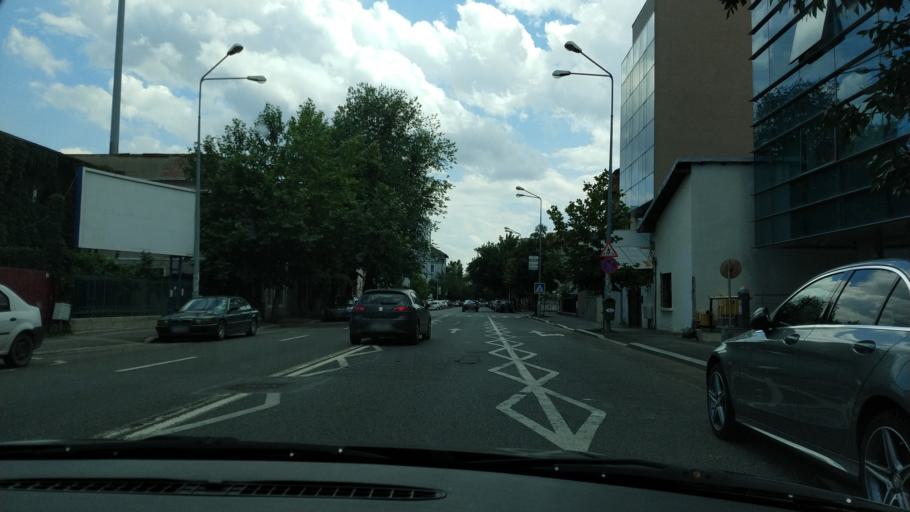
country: RO
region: Bucuresti
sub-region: Municipiul Bucuresti
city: Bucharest
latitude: 44.4564
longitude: 26.1006
